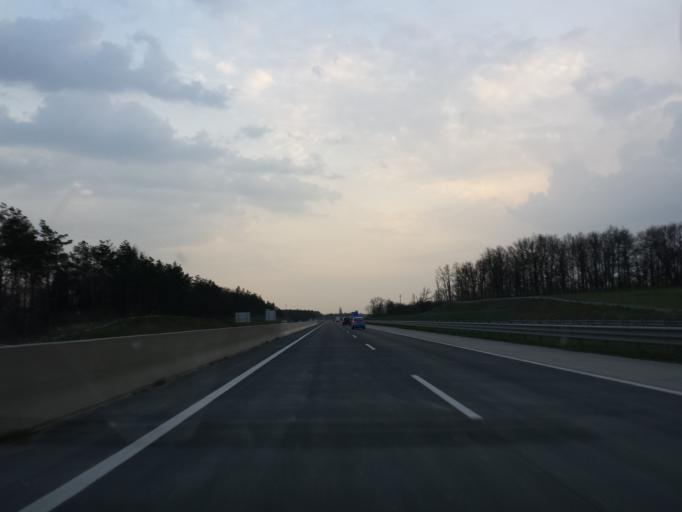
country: AT
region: Lower Austria
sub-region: Politischer Bezirk Mistelbach
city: Wolkersdorf im Weinviertel
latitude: 48.4148
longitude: 16.5401
